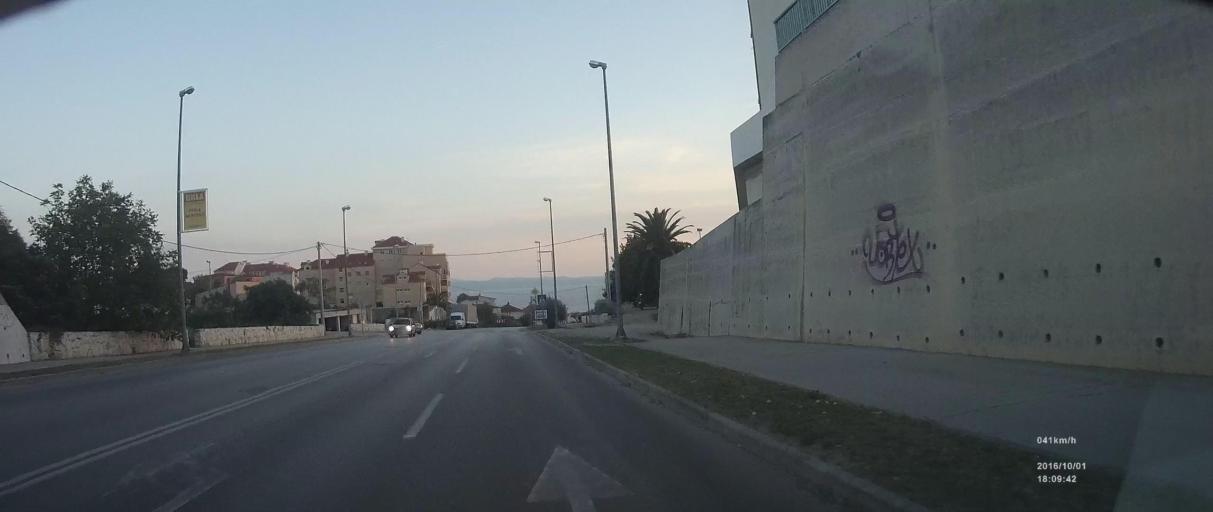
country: HR
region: Splitsko-Dalmatinska
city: Kamen
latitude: 43.5095
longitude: 16.4903
